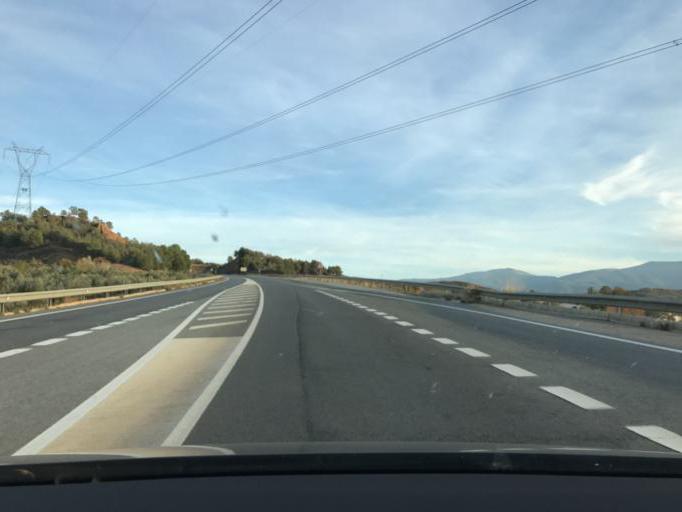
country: ES
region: Andalusia
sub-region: Provincia de Granada
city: Guadix
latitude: 37.2738
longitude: -3.1088
